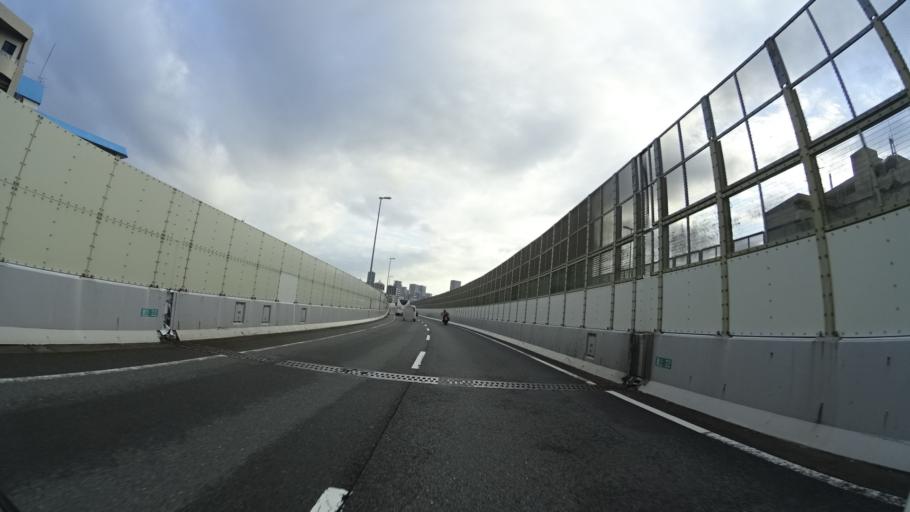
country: JP
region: Osaka
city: Osaka-shi
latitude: 34.6701
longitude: 135.4663
